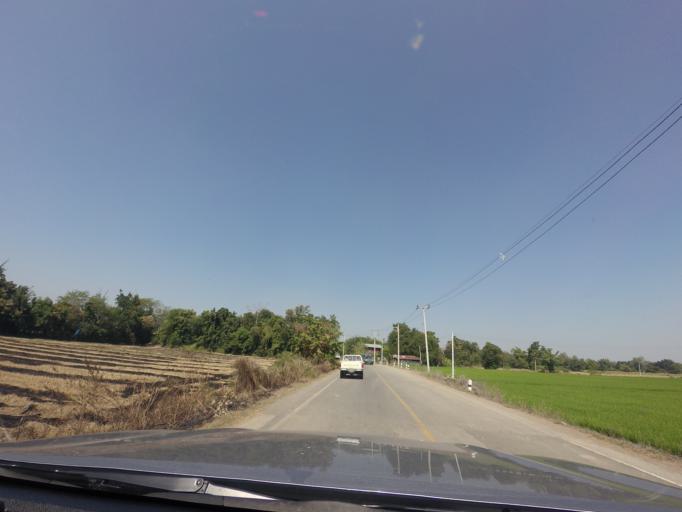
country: TH
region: Sukhothai
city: Si Samrong
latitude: 17.1628
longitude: 99.7703
